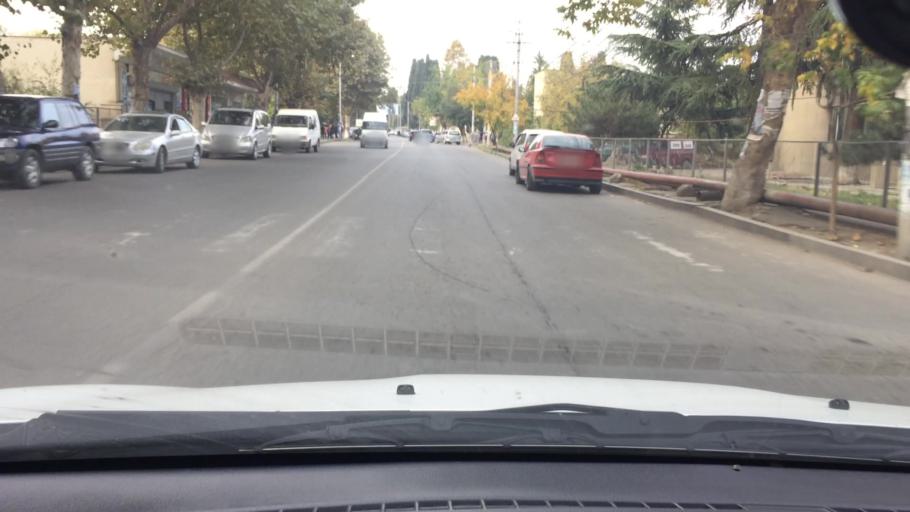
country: GE
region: Kvemo Kartli
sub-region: Marneuli
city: Marneuli
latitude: 41.4703
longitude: 44.8165
